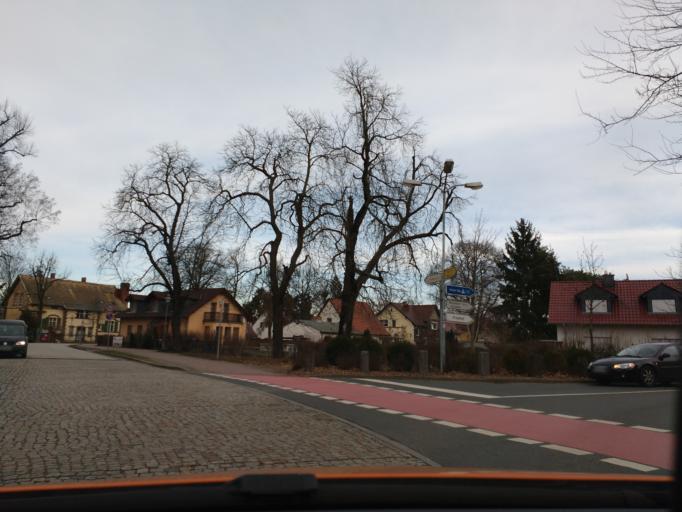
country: DE
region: Brandenburg
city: Michendorf
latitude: 52.3485
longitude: 13.0015
